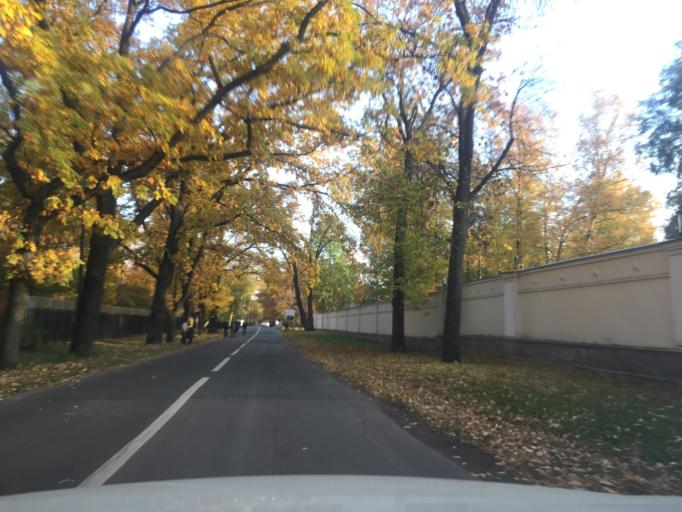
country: RU
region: St.-Petersburg
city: Novaya Derevnya
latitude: 59.9794
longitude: 30.2817
